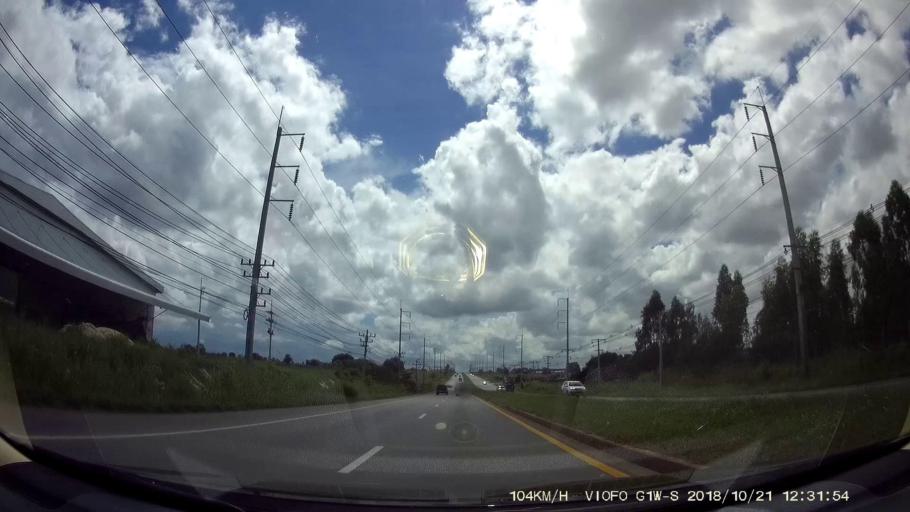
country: TH
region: Nakhon Ratchasima
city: Dan Khun Thot
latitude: 15.1496
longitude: 101.7328
